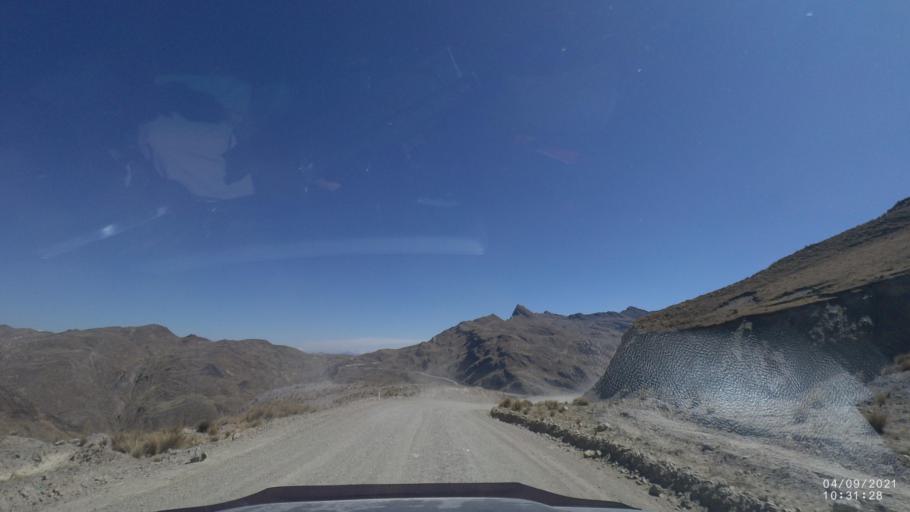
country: BO
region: Cochabamba
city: Sipe Sipe
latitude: -17.3015
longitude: -66.4464
